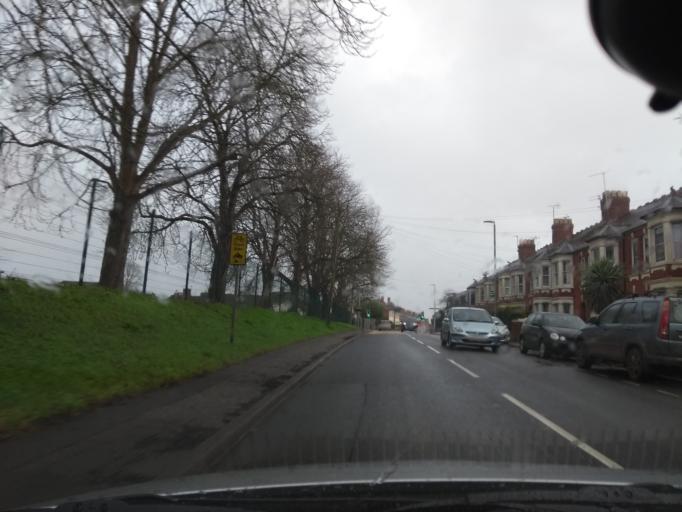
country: GB
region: England
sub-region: Somerset
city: Taunton
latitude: 51.0278
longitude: -3.1119
